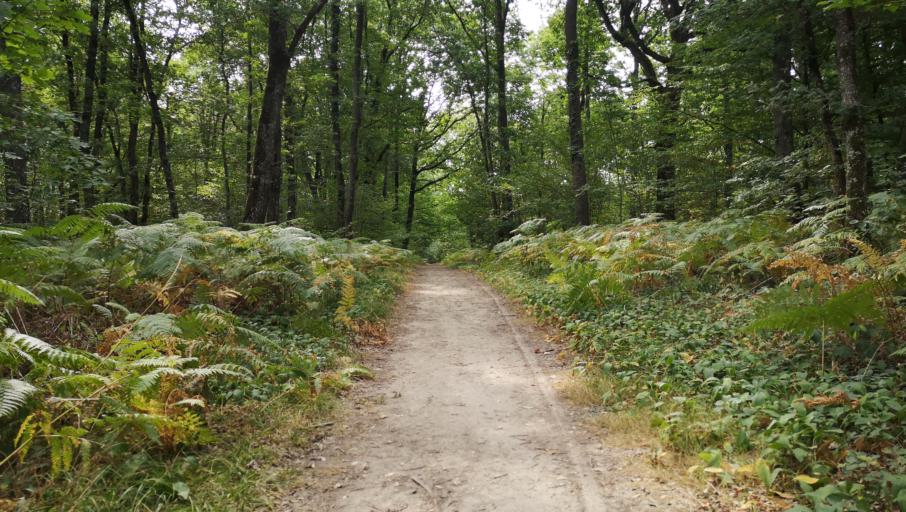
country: FR
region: Centre
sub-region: Departement du Loiret
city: Chanteau
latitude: 47.9438
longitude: 1.9866
